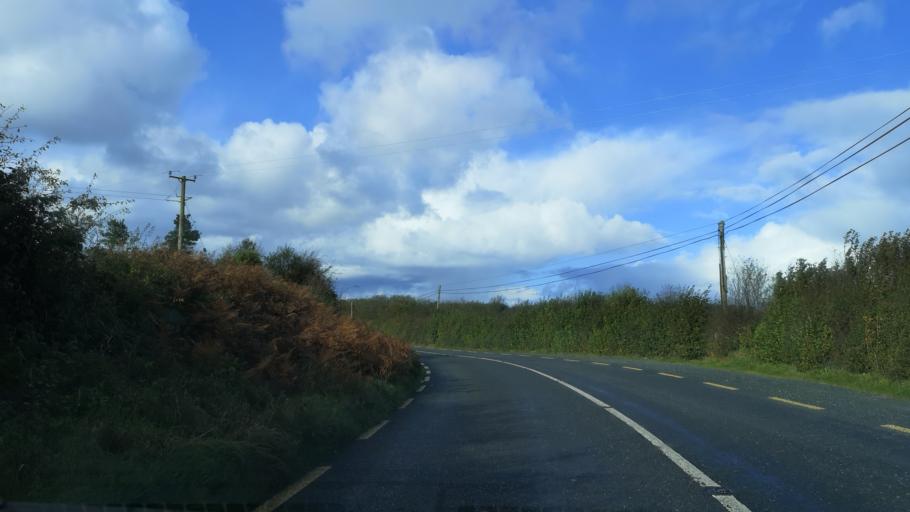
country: IE
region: Connaught
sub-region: Maigh Eo
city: Westport
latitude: 53.7871
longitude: -9.4588
